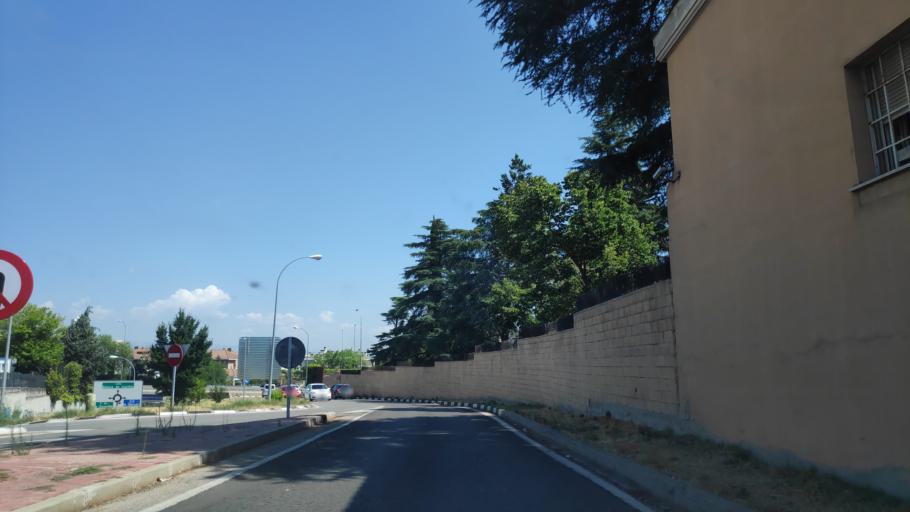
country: ES
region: Madrid
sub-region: Provincia de Madrid
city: Pozuelo de Alarcon
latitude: 40.4623
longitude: -3.7838
